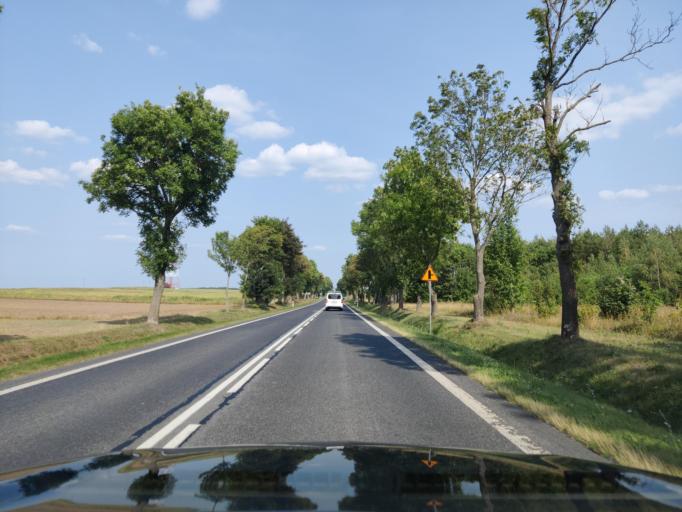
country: PL
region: Masovian Voivodeship
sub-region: Powiat makowski
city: Rzewnie
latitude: 52.8714
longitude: 21.3459
